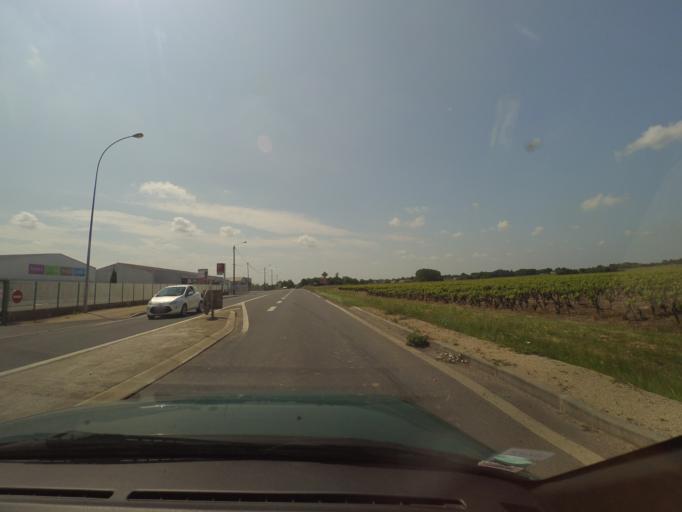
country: FR
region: Pays de la Loire
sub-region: Departement de la Loire-Atlantique
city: Mouzillon
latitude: 47.1251
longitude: -1.2825
